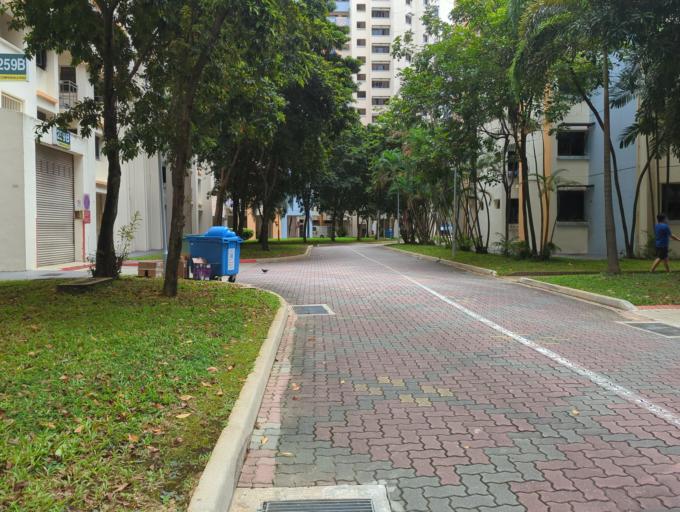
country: MY
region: Johor
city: Kampung Pasir Gudang Baru
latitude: 1.3938
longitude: 103.8971
